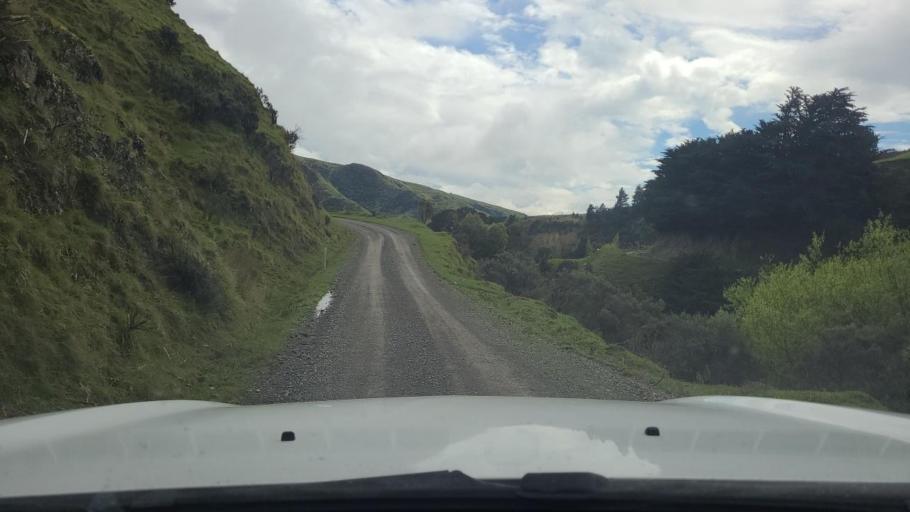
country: NZ
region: Wellington
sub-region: South Wairarapa District
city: Waipawa
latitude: -41.3672
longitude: 175.3928
